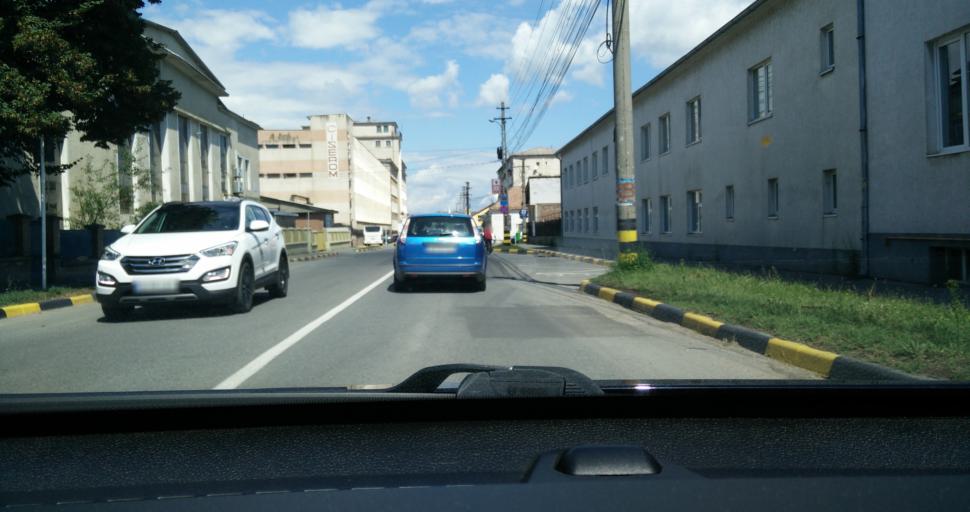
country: RO
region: Alba
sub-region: Municipiul Sebes
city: Sebes
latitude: 45.9494
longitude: 23.5655
